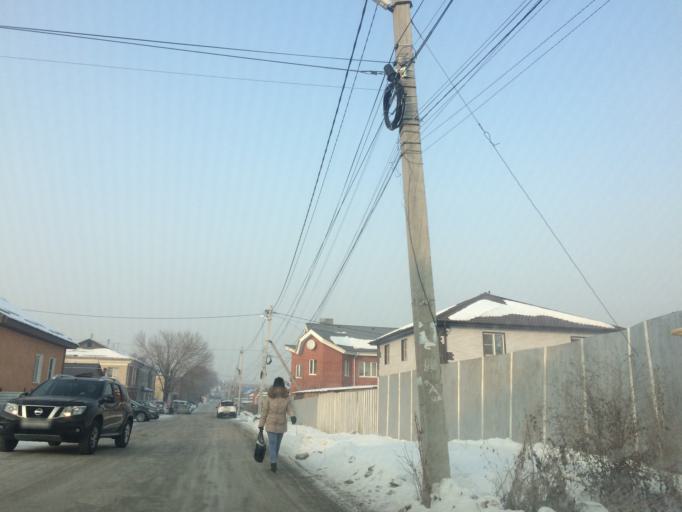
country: RU
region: Chelyabinsk
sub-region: Gorod Magnitogorsk
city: Magnitogorsk
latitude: 53.4188
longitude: 58.9641
